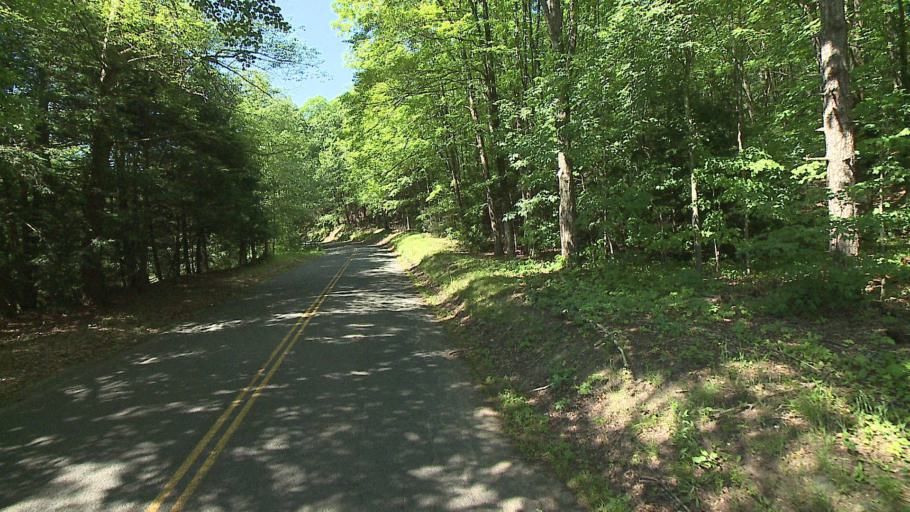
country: US
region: Connecticut
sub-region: Hartford County
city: Collinsville
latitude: 41.7689
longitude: -72.9554
